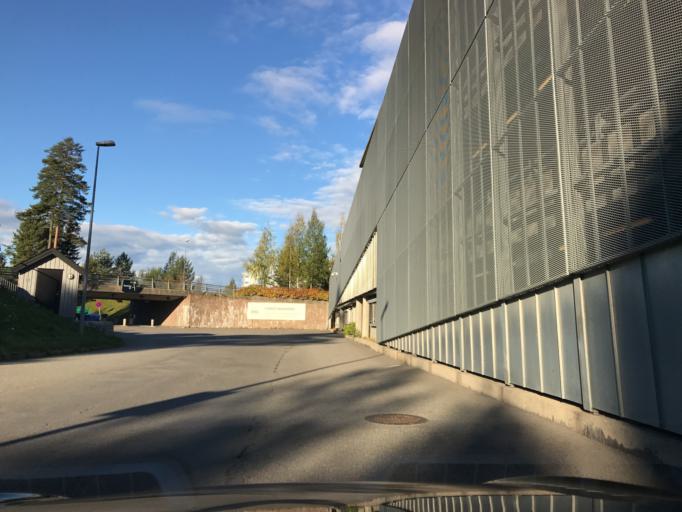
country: NO
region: Akershus
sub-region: Nannestad
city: Teigebyen
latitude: 60.1914
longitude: 11.0990
